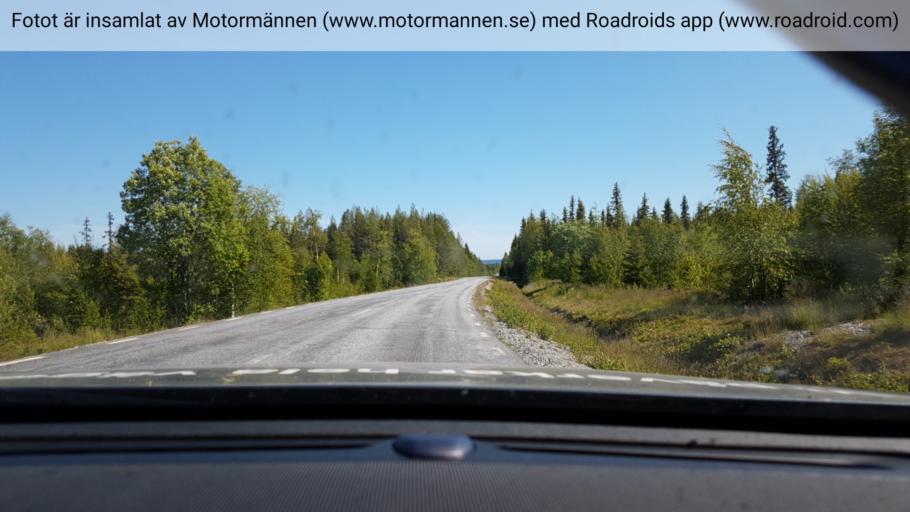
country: SE
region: Vaesterbotten
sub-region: Vilhelmina Kommun
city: Sjoberg
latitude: 64.7804
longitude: 16.1218
